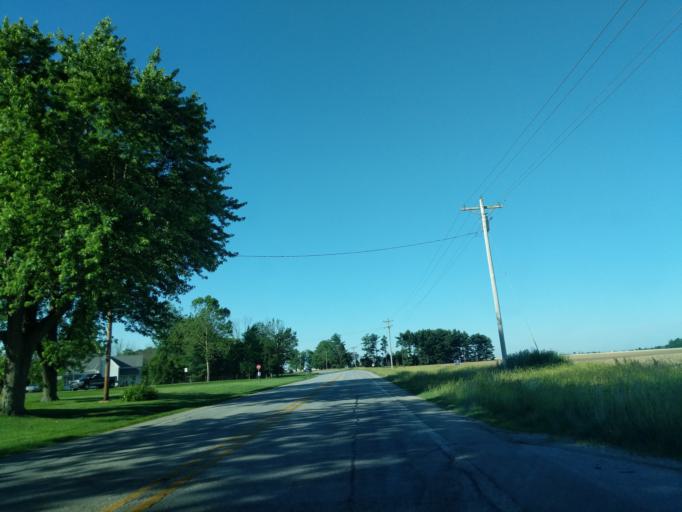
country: US
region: Indiana
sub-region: Shelby County
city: Shelbyville
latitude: 39.5990
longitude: -85.7752
